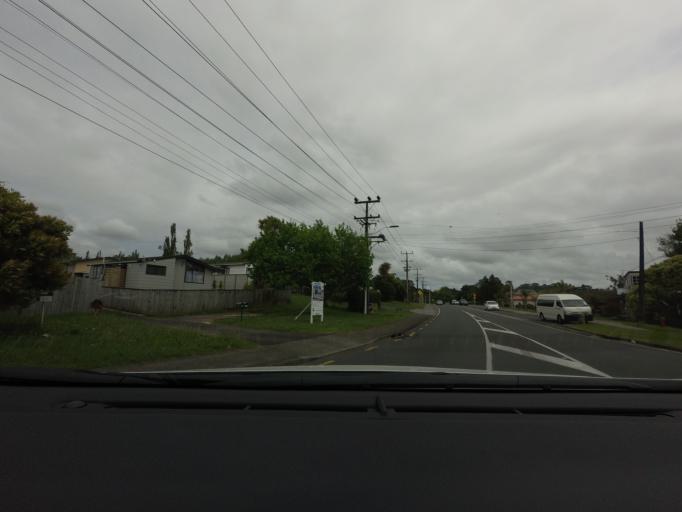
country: NZ
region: Auckland
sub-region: Auckland
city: Waitakere
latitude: -36.8981
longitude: 174.6128
